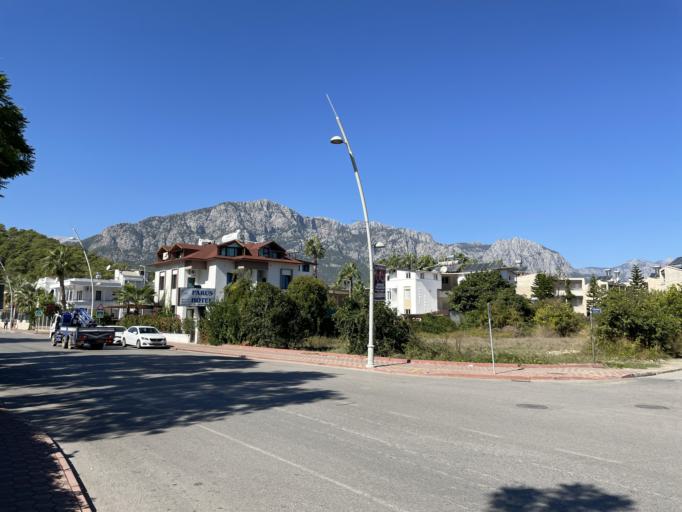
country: TR
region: Antalya
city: Kemer
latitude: 36.5968
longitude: 30.5655
